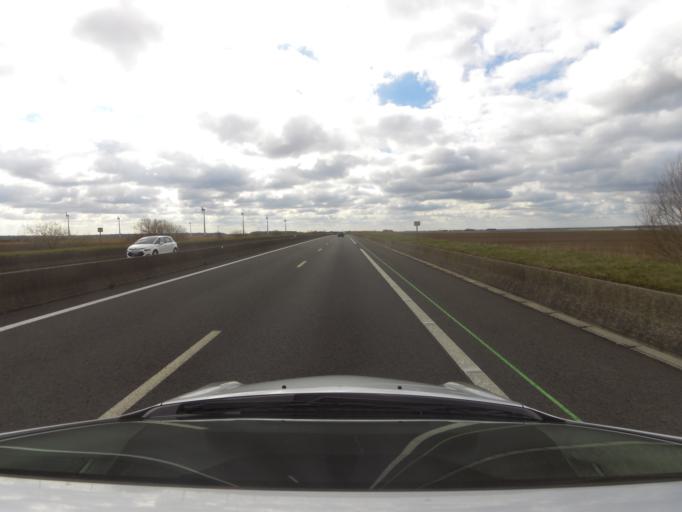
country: FR
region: Picardie
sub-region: Departement de la Somme
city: Rue
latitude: 50.3152
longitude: 1.7218
